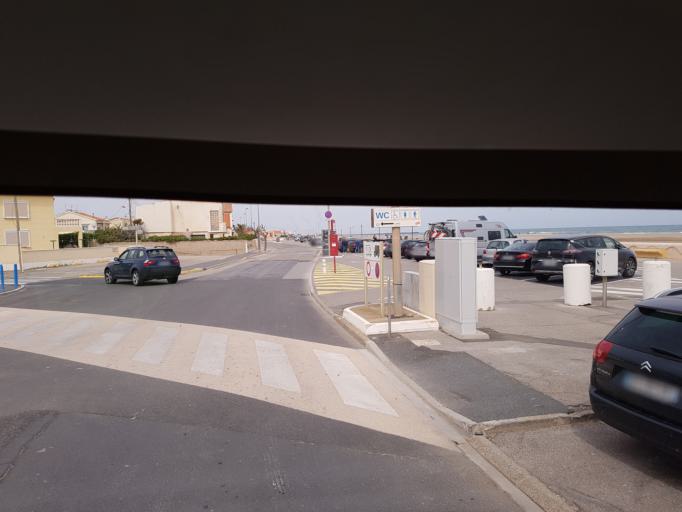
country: FR
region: Languedoc-Roussillon
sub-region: Departement de l'Aude
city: Armissan
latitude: 43.1599
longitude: 3.1686
